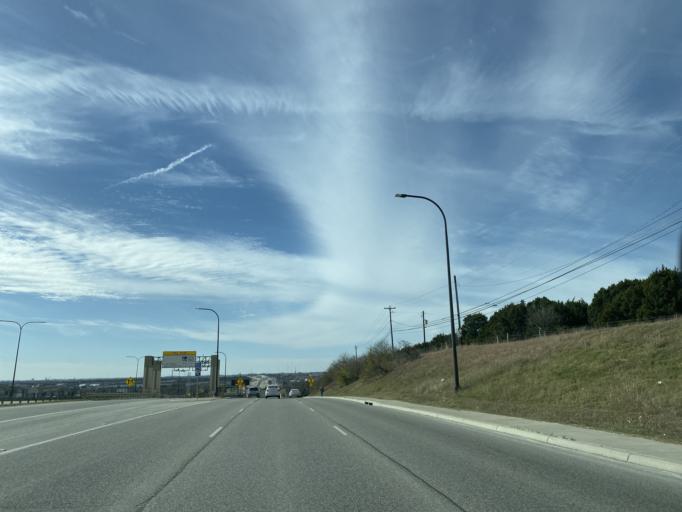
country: US
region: Texas
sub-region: Travis County
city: Manor
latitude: 30.3304
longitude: -97.6357
